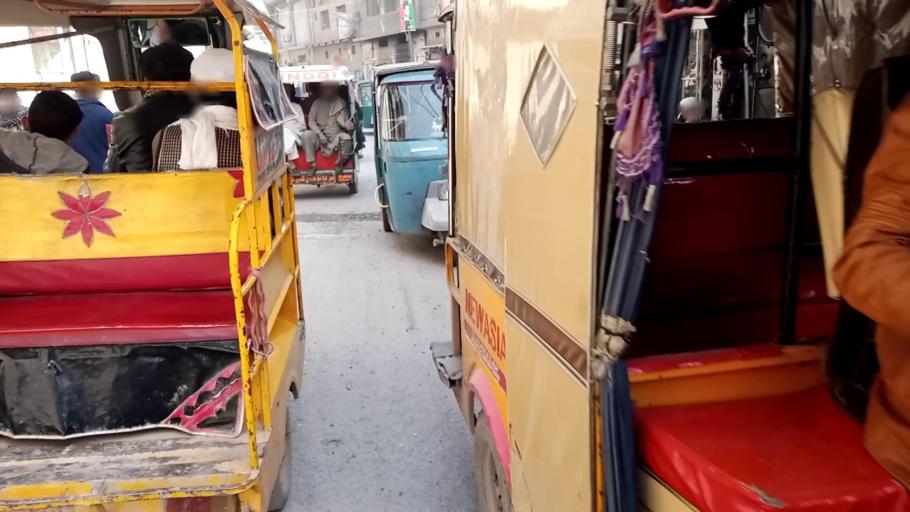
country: PK
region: Khyber Pakhtunkhwa
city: Peshawar
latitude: 34.0022
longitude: 71.5780
